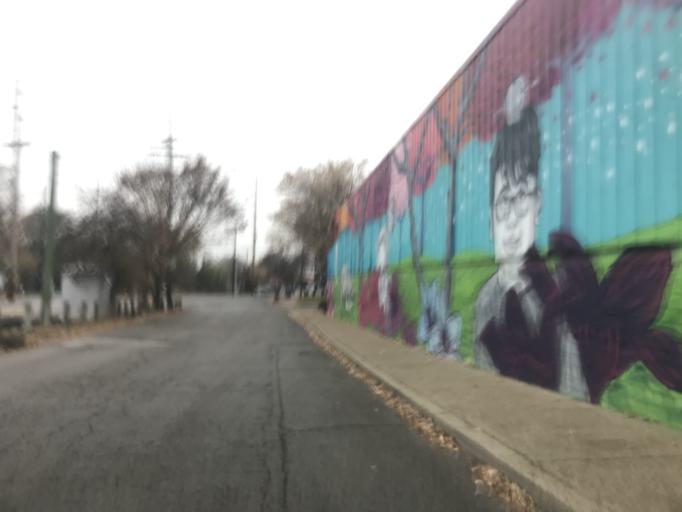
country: US
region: Indiana
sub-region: Clark County
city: Jeffersonville
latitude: 38.2540
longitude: -85.7065
